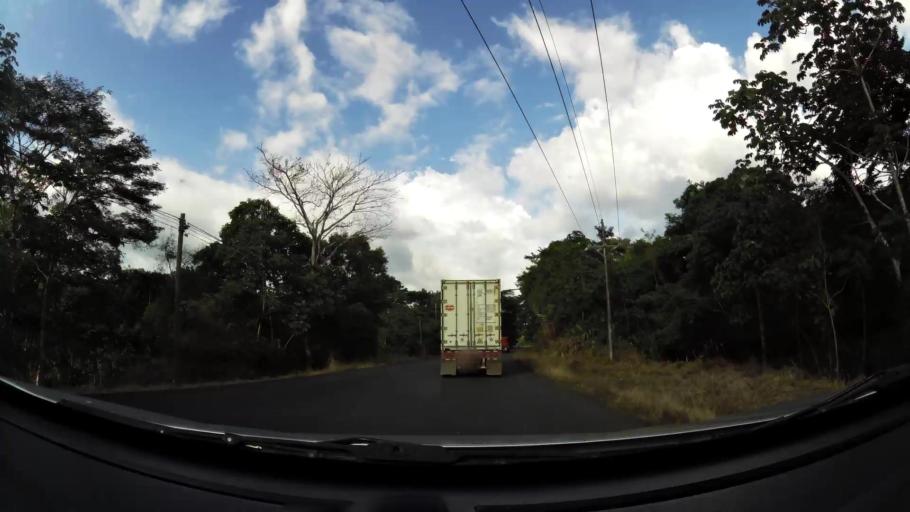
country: CR
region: Puntarenas
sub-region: Canton de Garabito
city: Jaco
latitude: 9.7655
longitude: -84.6135
